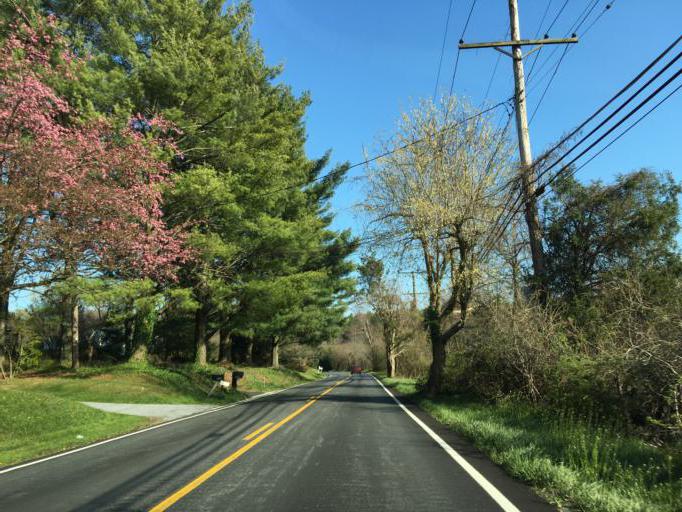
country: US
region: Maryland
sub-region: Baltimore County
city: Hampton
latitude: 39.5039
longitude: -76.5334
